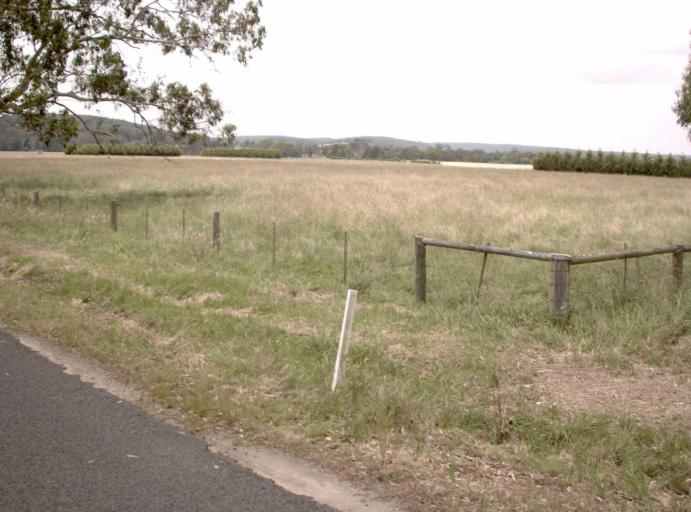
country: AU
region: Victoria
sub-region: Latrobe
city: Traralgon
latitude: -38.4867
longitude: 146.6806
